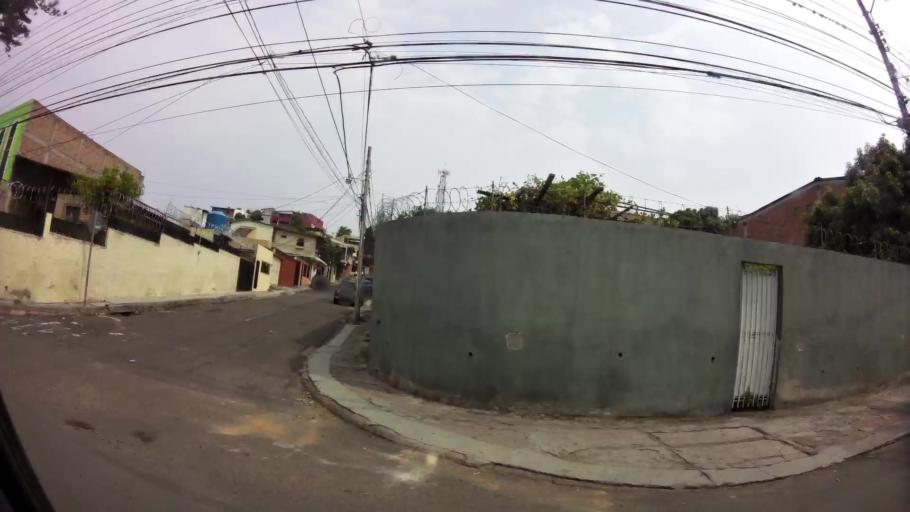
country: HN
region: Francisco Morazan
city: Tegucigalpa
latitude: 14.0726
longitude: -87.1899
